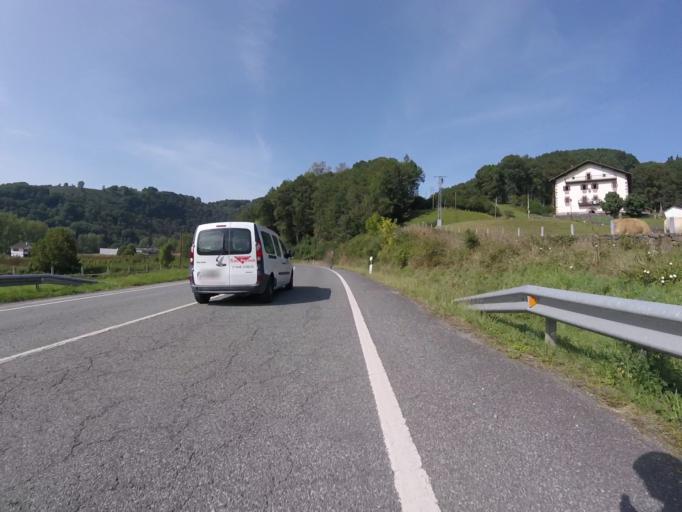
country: ES
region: Navarre
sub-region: Provincia de Navarra
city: Doneztebe
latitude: 43.1428
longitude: -1.5698
